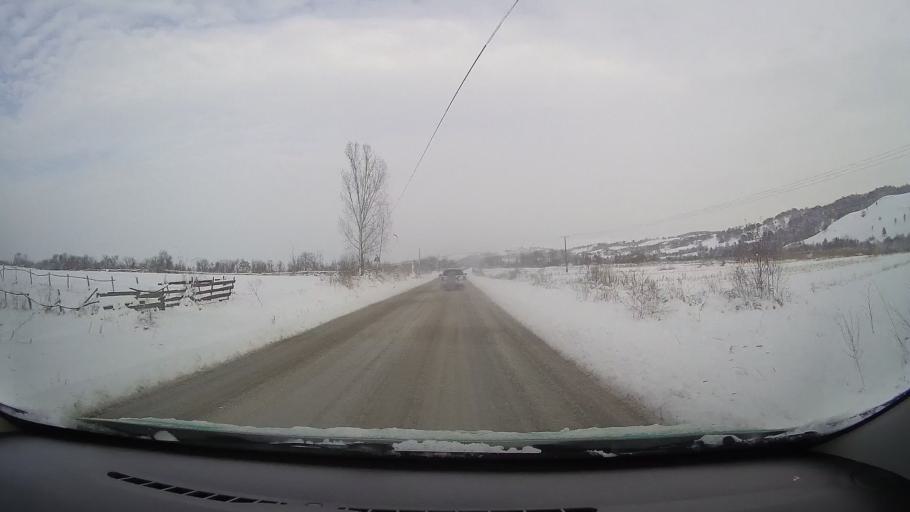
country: RO
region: Alba
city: Pianu de Sus
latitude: 45.9125
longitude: 23.4814
